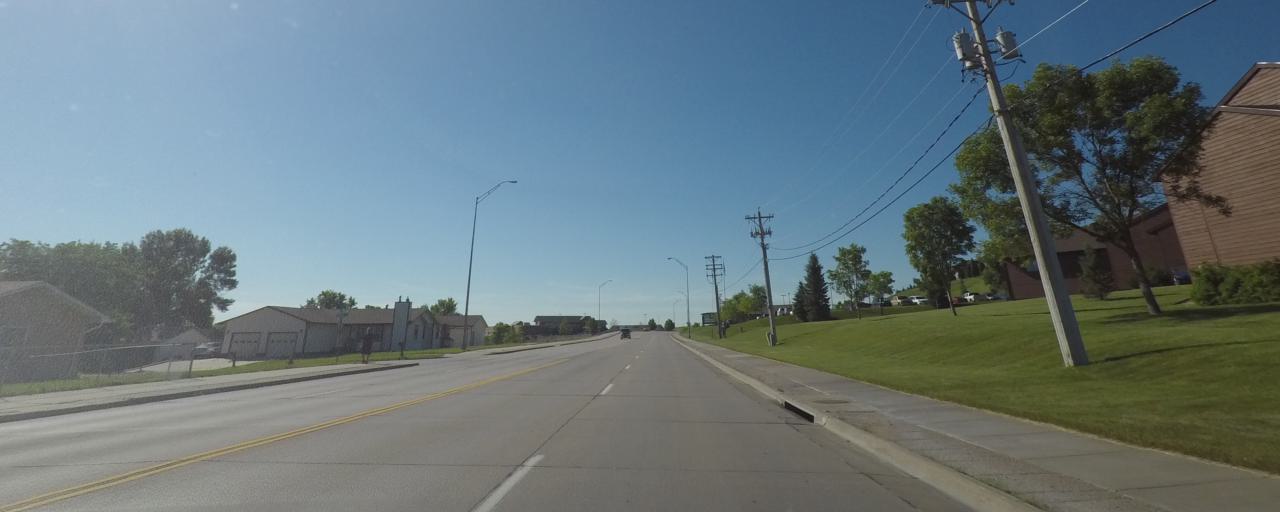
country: US
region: South Dakota
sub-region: Pennington County
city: Rapid City
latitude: 44.0465
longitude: -103.2215
